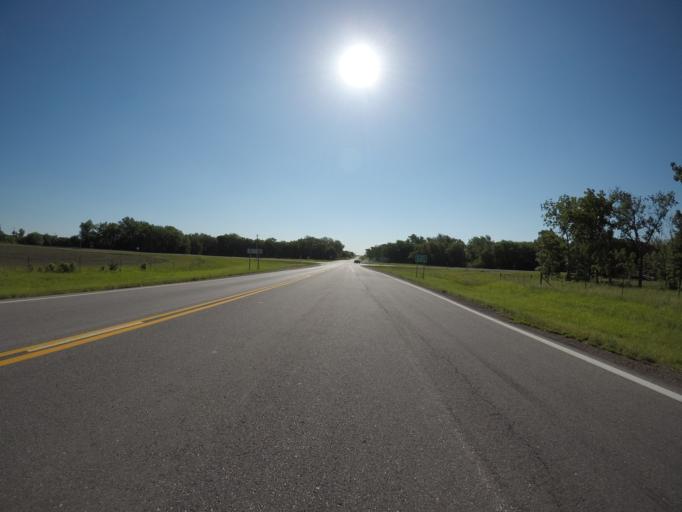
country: US
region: Kansas
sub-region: Lyon County
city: Emporia
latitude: 38.6519
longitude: -96.0992
